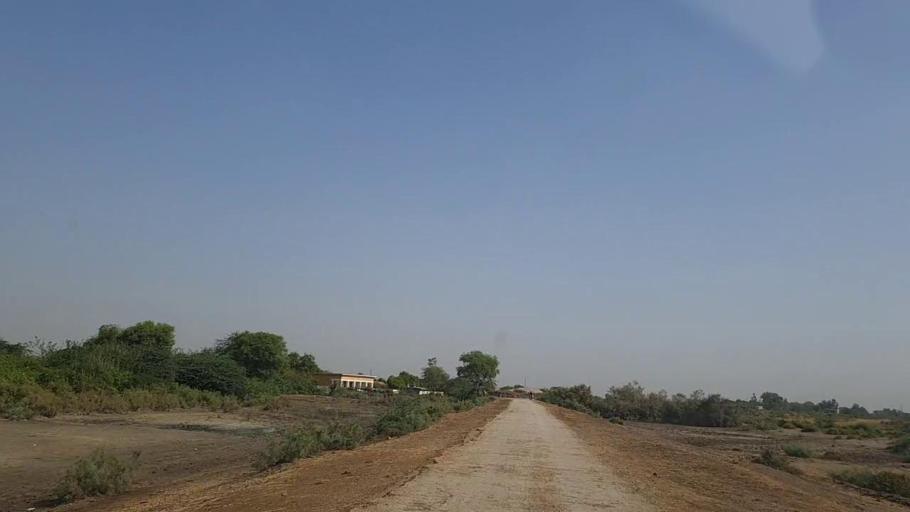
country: PK
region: Sindh
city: Thatta
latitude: 24.6851
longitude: 68.0470
